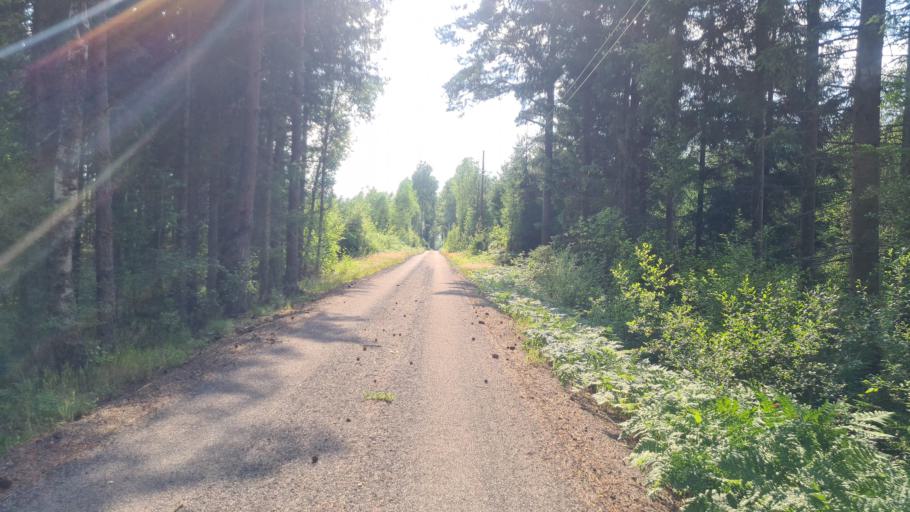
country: SE
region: Kronoberg
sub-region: Ljungby Kommun
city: Lagan
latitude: 56.8566
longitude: 14.1217
